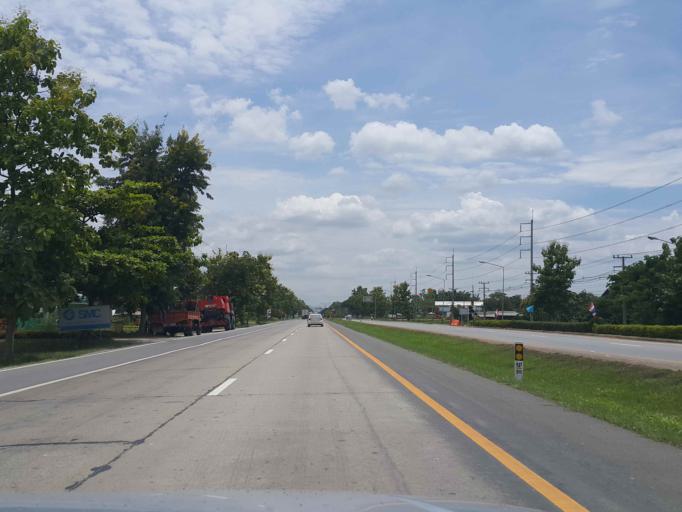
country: TH
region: Lamphun
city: Ban Thi
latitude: 18.6391
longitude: 99.0524
